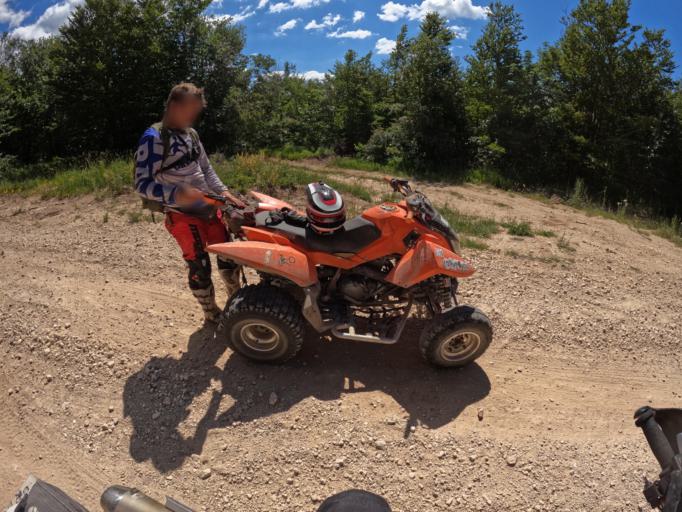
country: BA
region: Federation of Bosnia and Herzegovina
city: Vidosi
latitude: 43.8315
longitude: 17.1384
